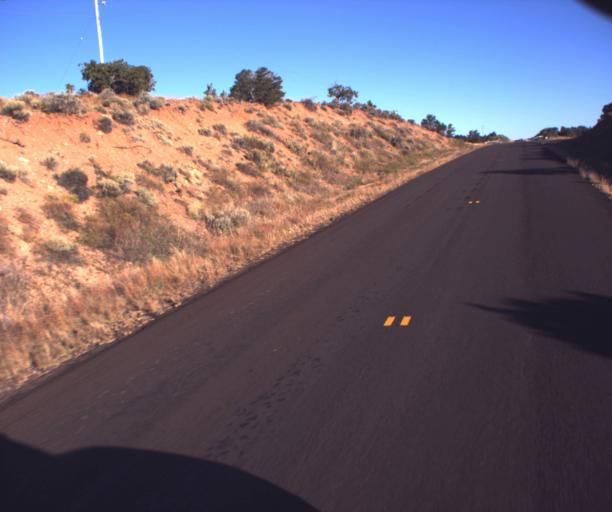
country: US
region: Arizona
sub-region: Apache County
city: Ganado
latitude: 35.5663
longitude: -109.5339
